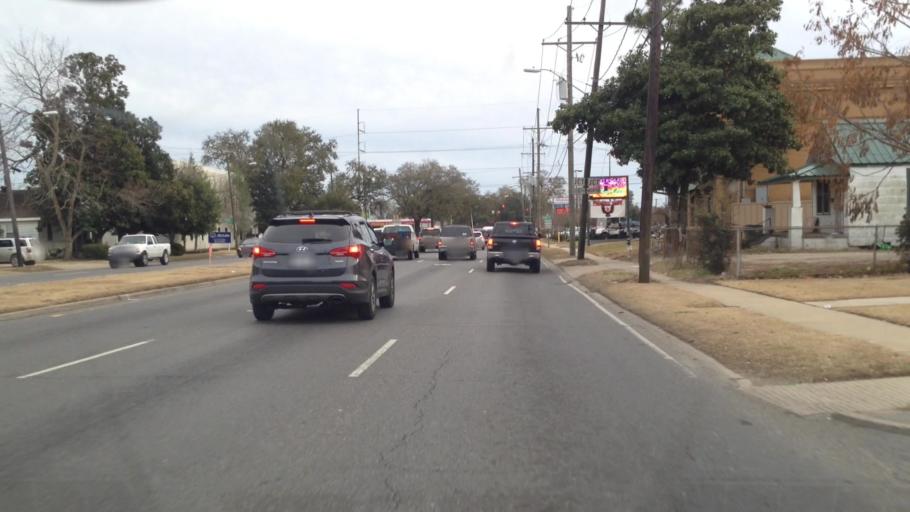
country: US
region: Louisiana
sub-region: Jefferson Parish
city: Metairie Terrace
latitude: 29.9775
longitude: -90.1788
